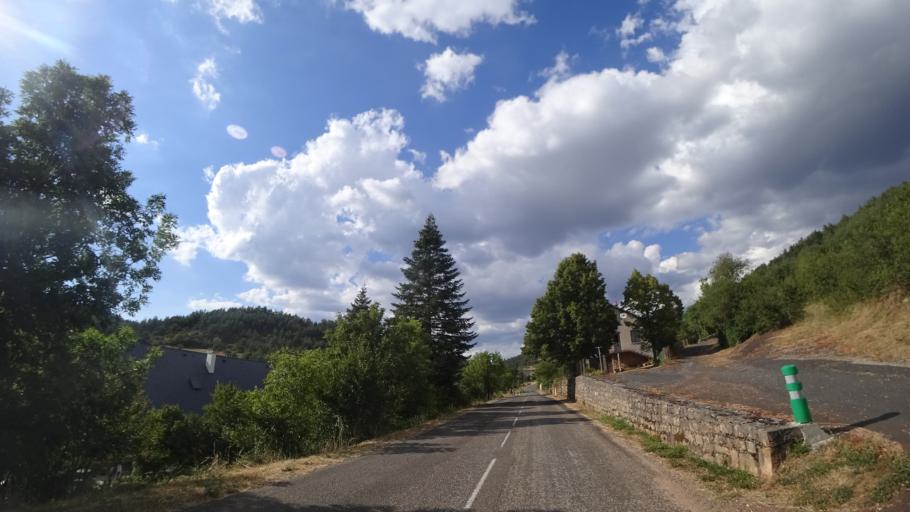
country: FR
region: Languedoc-Roussillon
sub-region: Departement de la Lozere
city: Chanac
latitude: 44.3553
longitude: 3.3535
